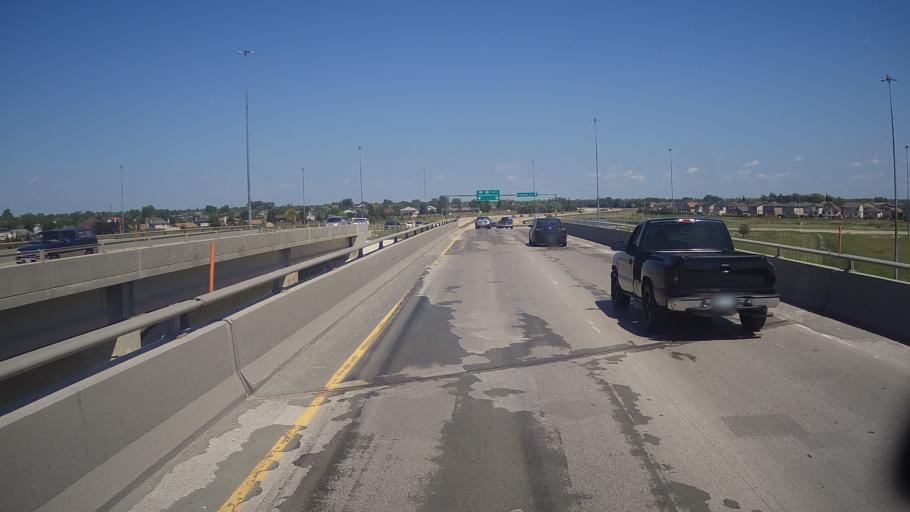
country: CA
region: Manitoba
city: Winnipeg
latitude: 49.9105
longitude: -97.0566
